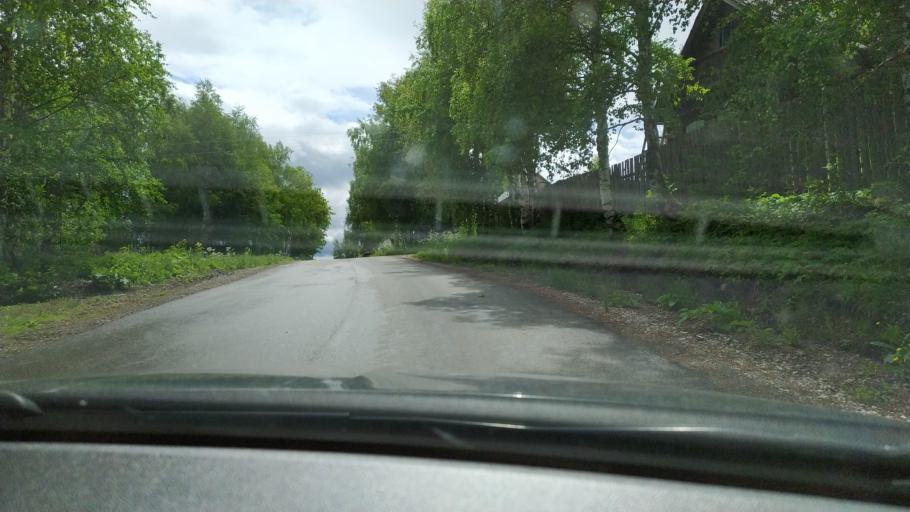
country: RU
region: Perm
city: Gremyachinsk
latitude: 58.5125
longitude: 57.8340
